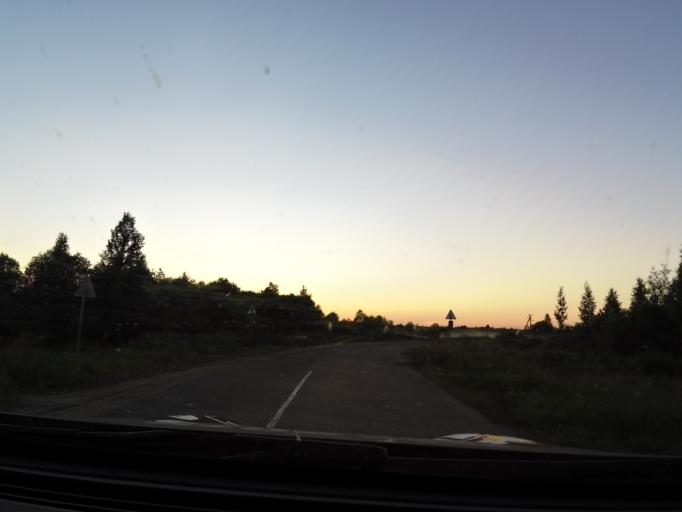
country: RU
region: Kostroma
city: Buy
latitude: 58.4076
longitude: 41.2408
